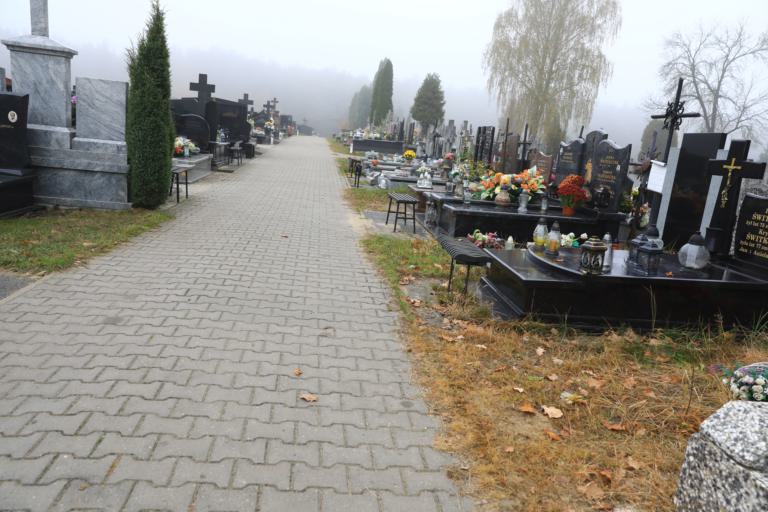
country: PL
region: Masovian Voivodeship
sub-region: Powiat wolominski
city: Nowe Lipiny
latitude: 52.3305
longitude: 21.2724
